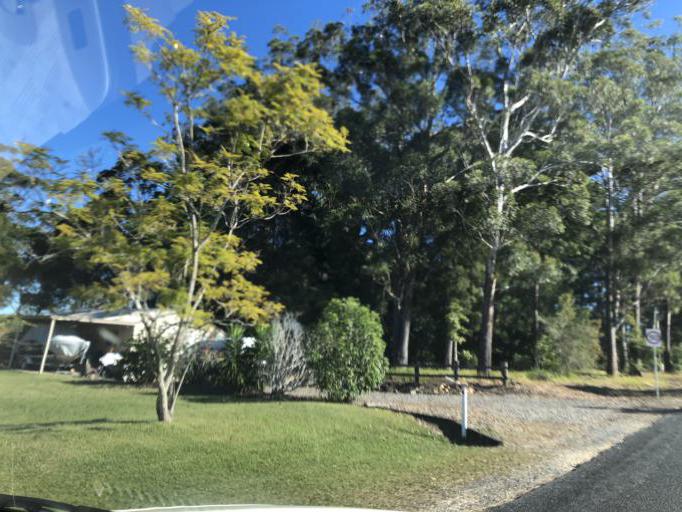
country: AU
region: New South Wales
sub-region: Nambucca Shire
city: Nambucca
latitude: -30.6795
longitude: 152.9630
